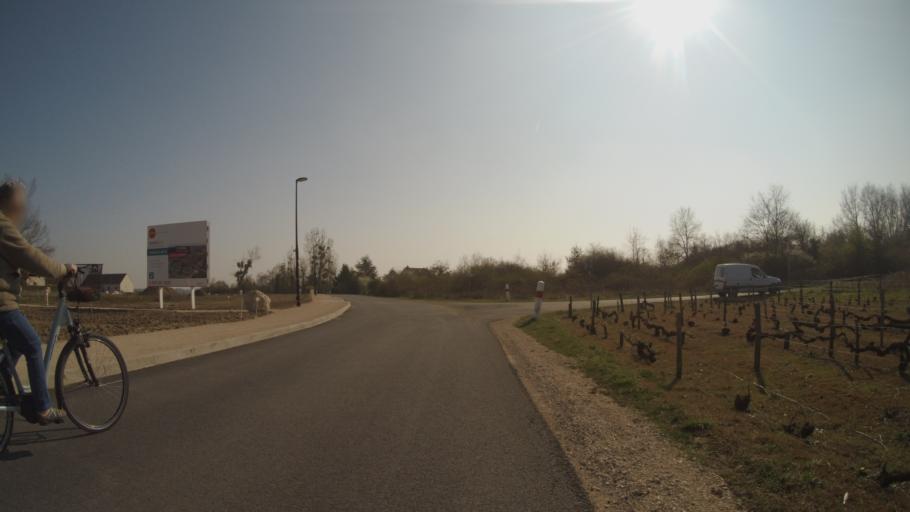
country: FR
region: Centre
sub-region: Departement du Loiret
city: Mardie
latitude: 47.8886
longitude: 2.0492
